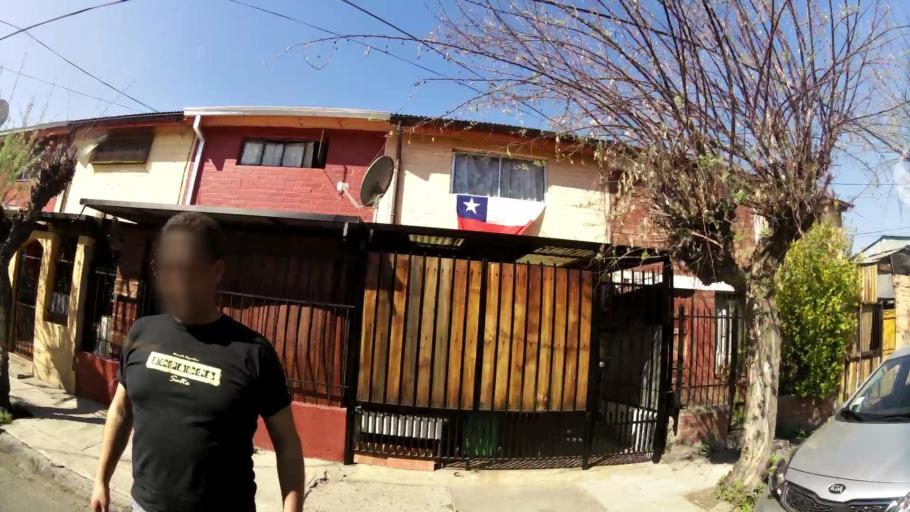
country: CL
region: Santiago Metropolitan
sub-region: Provincia de Santiago
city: La Pintana
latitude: -33.5590
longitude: -70.6255
